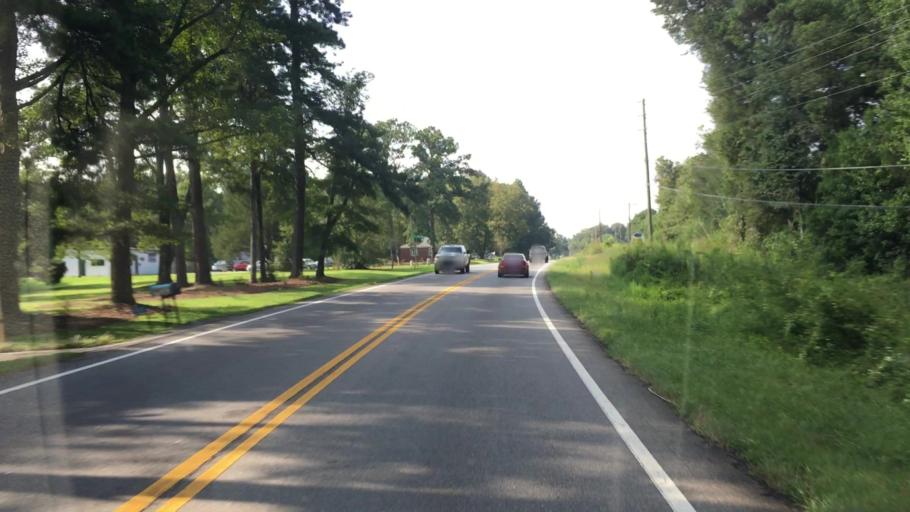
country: US
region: Georgia
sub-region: Walton County
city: Monroe
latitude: 33.7358
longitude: -83.7017
